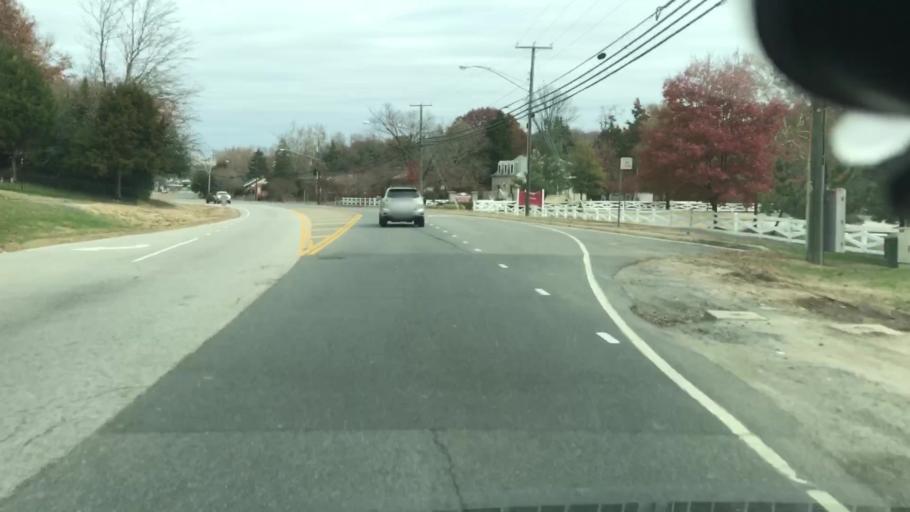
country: US
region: Virginia
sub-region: Fairfax County
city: Huntington
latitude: 38.7893
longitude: -77.0863
